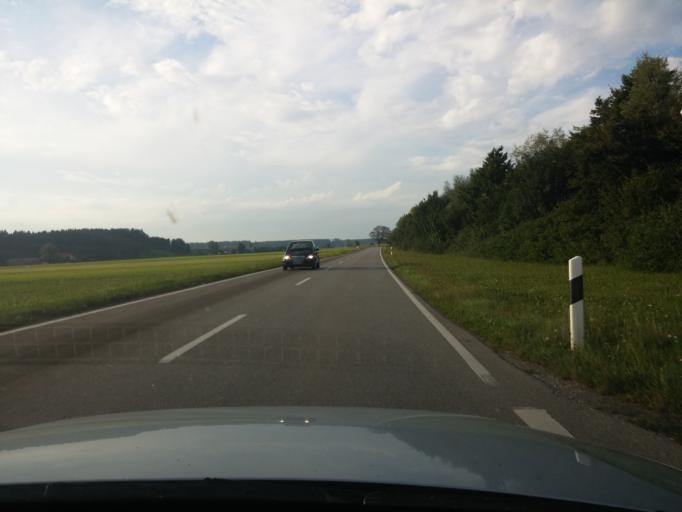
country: DE
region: Bavaria
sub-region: Swabia
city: Legau
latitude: 47.8697
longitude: 10.1253
